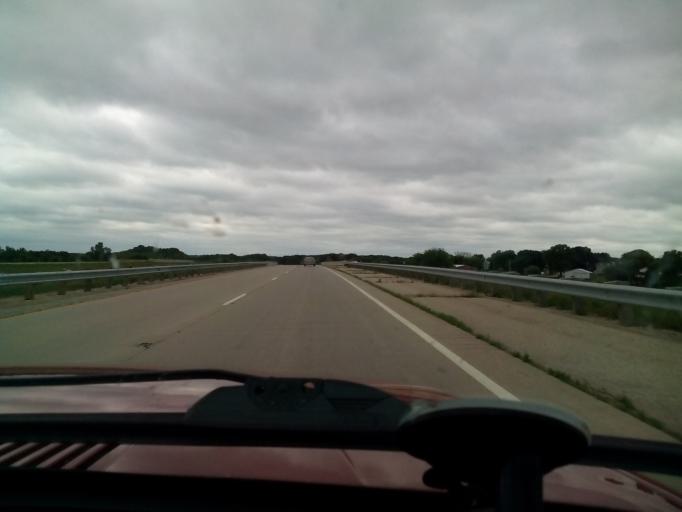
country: US
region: Wisconsin
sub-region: Dane County
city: Sun Prairie
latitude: 43.2423
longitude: -89.1456
